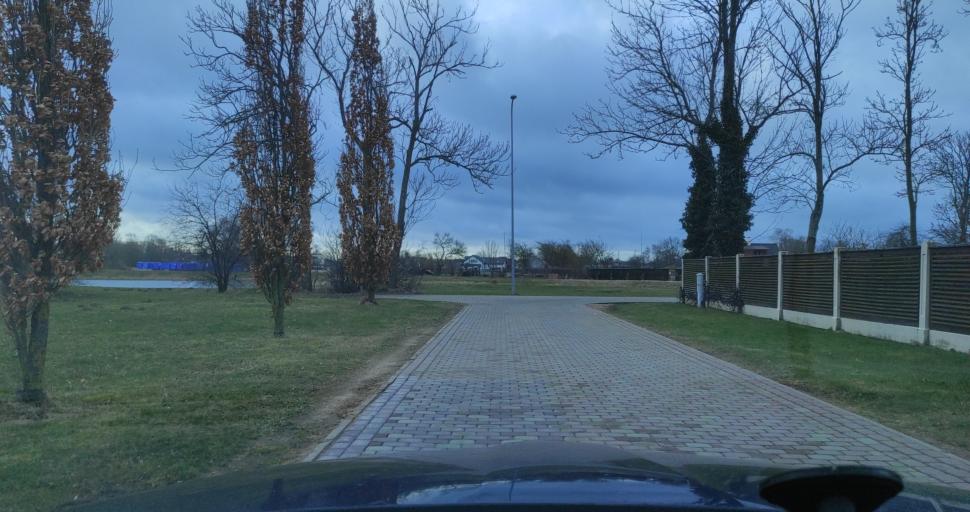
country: LV
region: Ventspils
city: Ventspils
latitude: 57.3839
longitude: 21.5727
